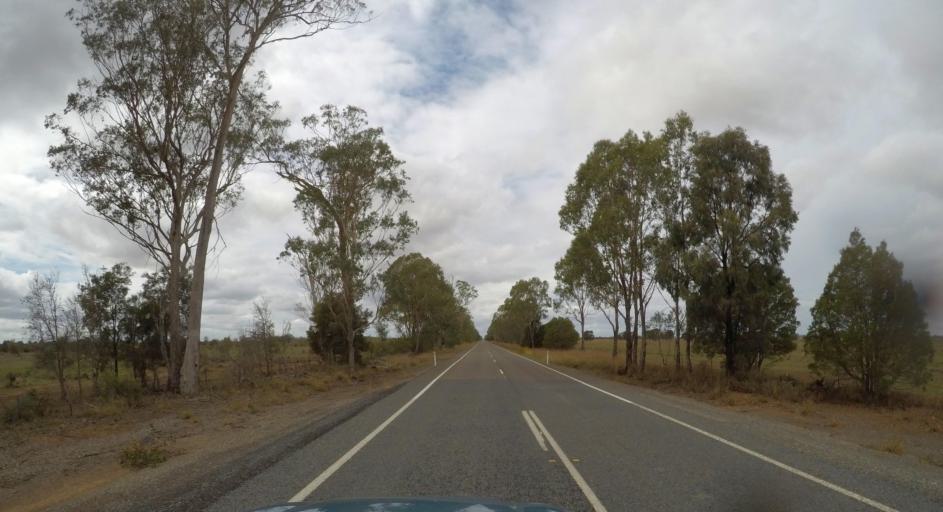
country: AU
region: Queensland
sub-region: South Burnett
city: Kingaroy
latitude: -26.3904
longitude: 151.2047
